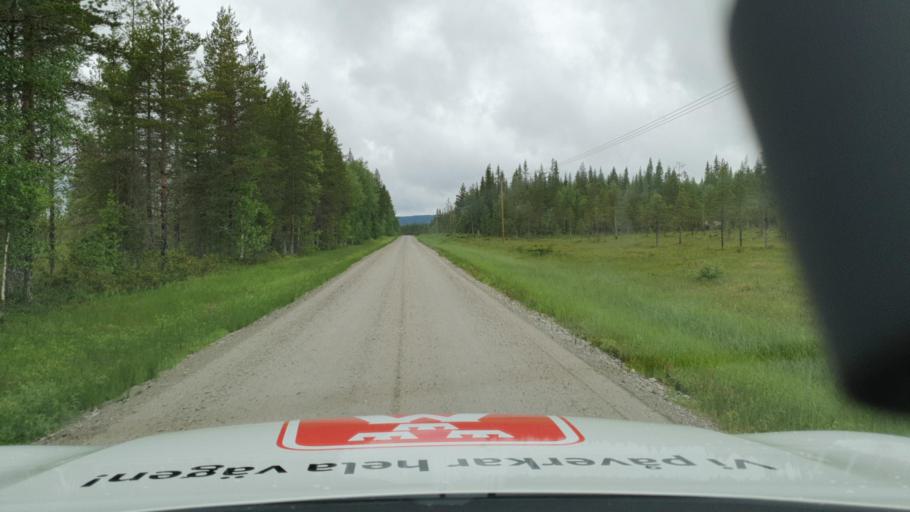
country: SE
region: Vaesterbotten
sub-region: Dorotea Kommun
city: Dorotea
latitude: 63.9835
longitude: 16.8208
